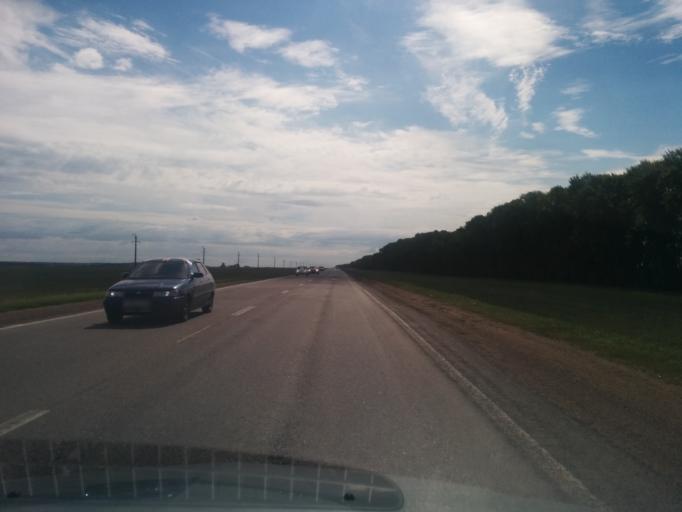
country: RU
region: Bashkortostan
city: Karmaskaly
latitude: 54.4194
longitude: 56.0470
